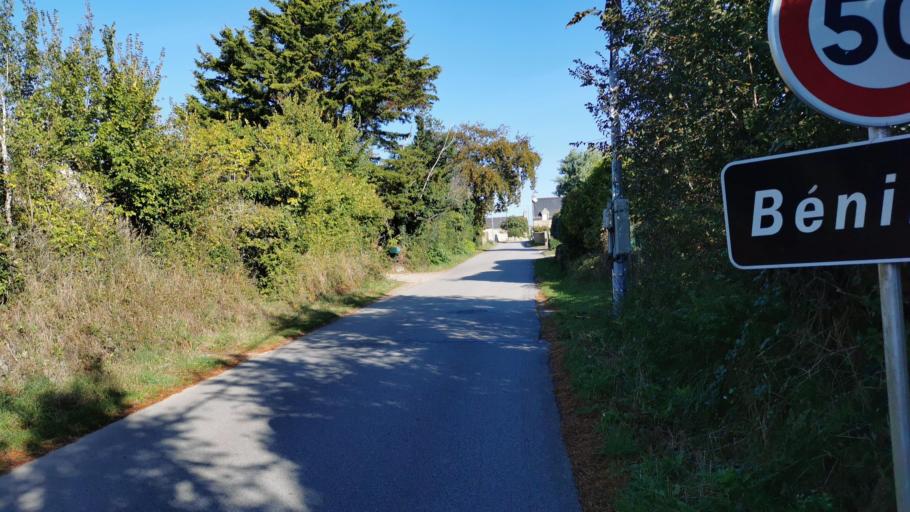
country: FR
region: Brittany
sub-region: Departement du Morbihan
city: Arzon
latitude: 47.5450
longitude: -2.8663
